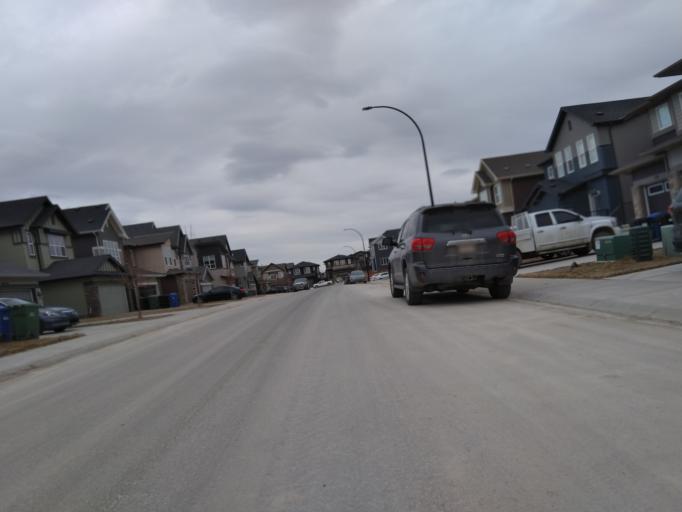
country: CA
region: Alberta
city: Airdrie
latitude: 51.1797
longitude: -114.0804
